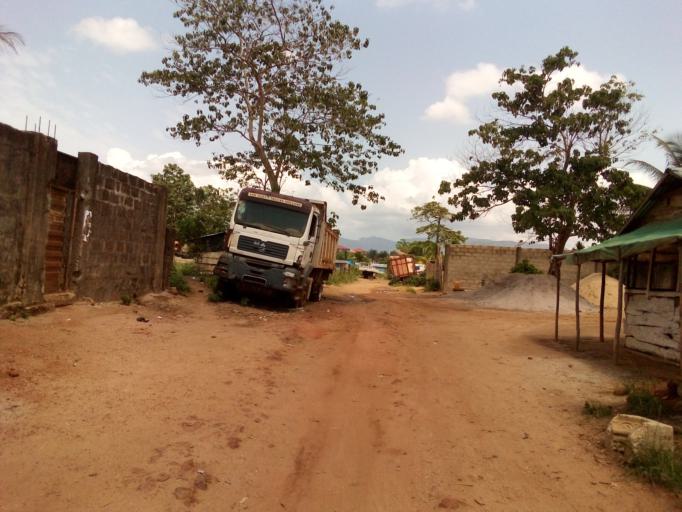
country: SL
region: Western Area
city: Waterloo
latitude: 8.3369
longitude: -13.0242
